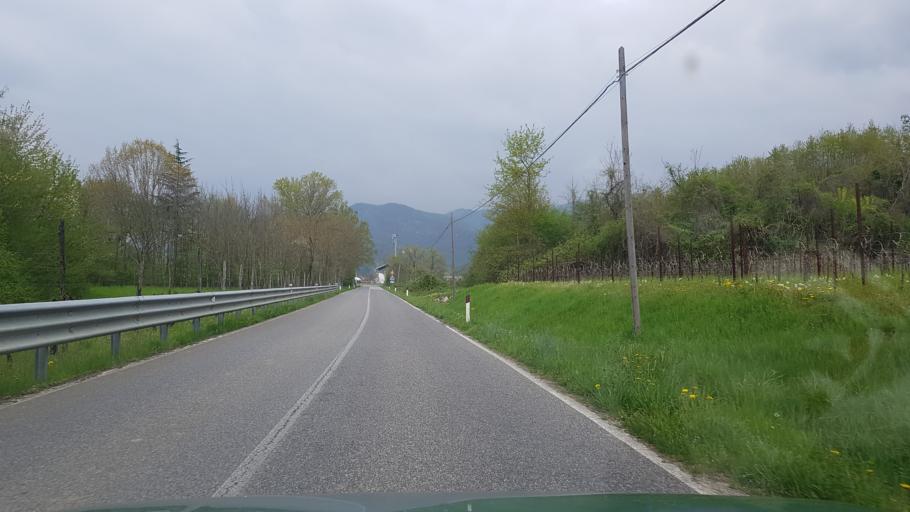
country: IT
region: Friuli Venezia Giulia
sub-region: Provincia di Udine
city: Faedis
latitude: 46.1363
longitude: 13.3510
